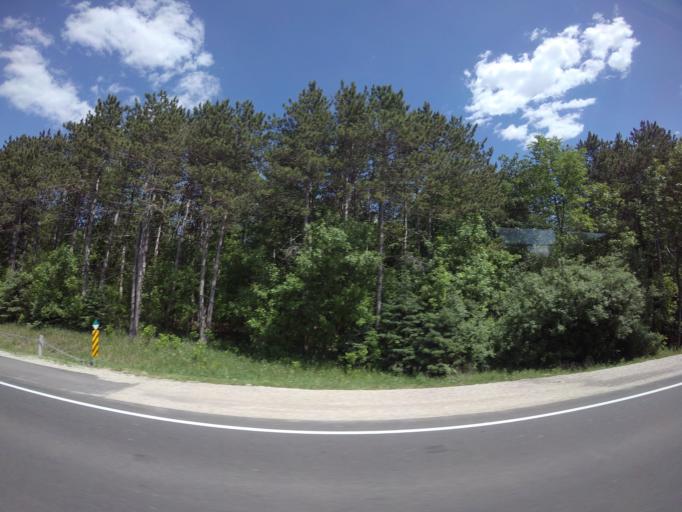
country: CA
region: Ontario
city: Carleton Place
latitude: 45.0836
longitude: -76.2447
